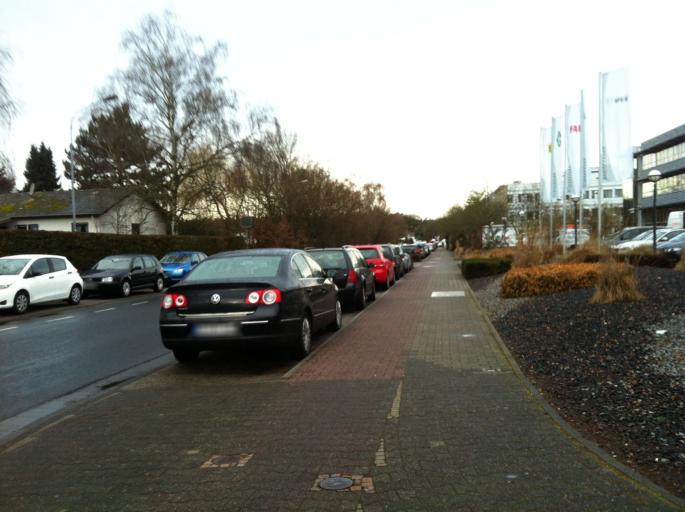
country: DE
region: Hesse
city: Langen
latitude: 50.0038
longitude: 8.6526
